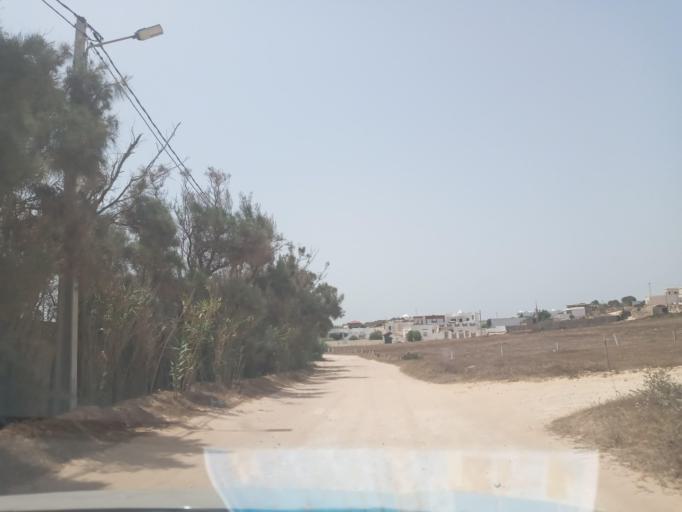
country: TN
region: Nabul
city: El Haouaria
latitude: 37.0299
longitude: 11.0564
